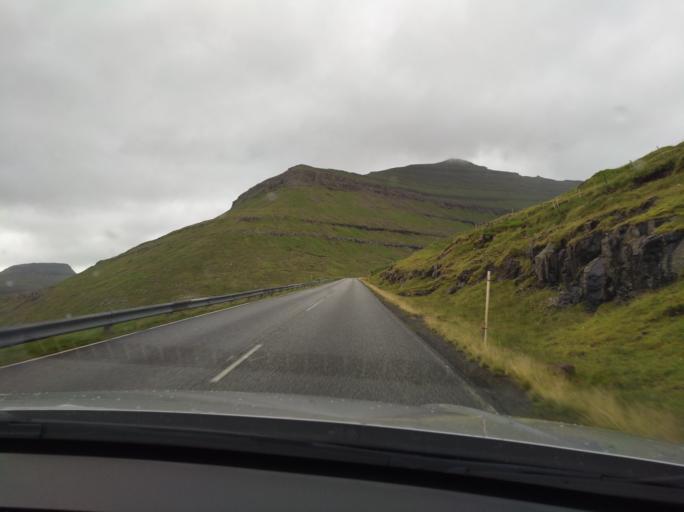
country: FO
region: Eysturoy
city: Fuglafjordur
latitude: 62.2218
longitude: -6.8745
